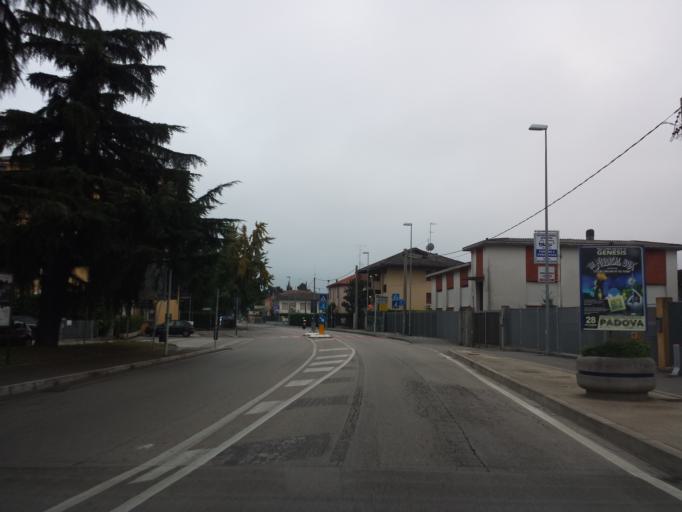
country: IT
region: Veneto
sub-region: Provincia di Padova
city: Padova
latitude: 45.4258
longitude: 11.8720
